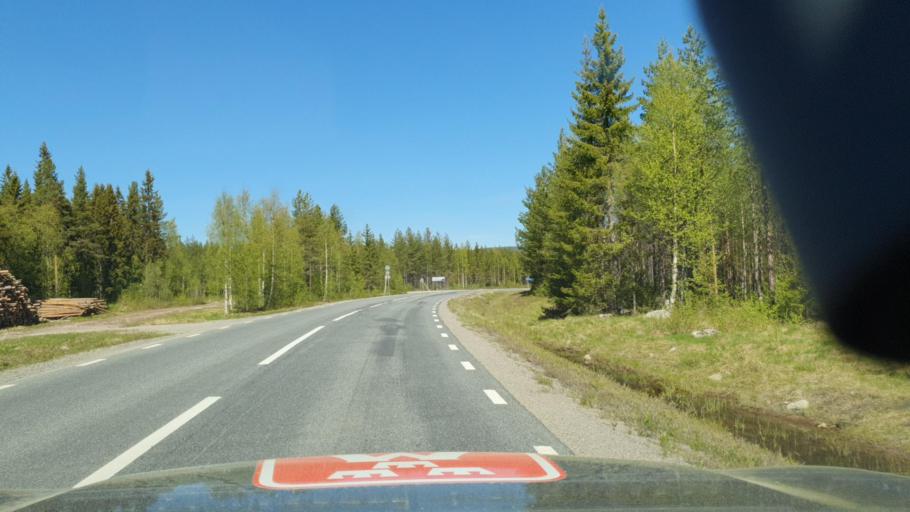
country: SE
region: Vaesternorrland
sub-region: OErnskoeldsviks Kommun
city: Bredbyn
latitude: 63.7594
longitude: 18.4789
